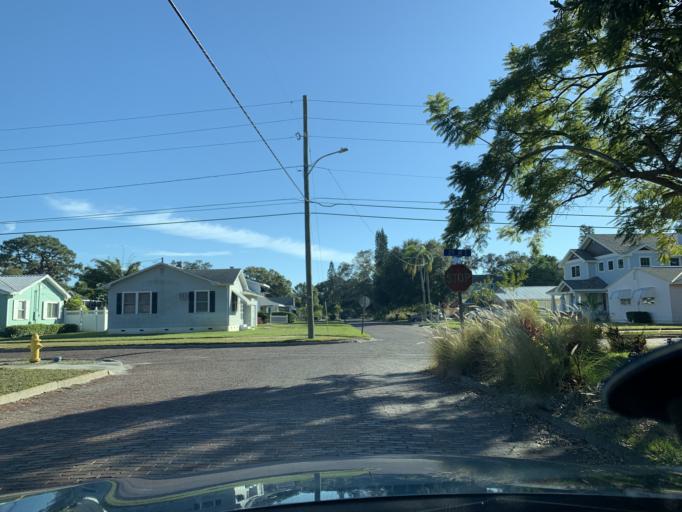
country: US
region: Florida
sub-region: Pinellas County
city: Gulfport
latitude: 27.7413
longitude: -82.7051
